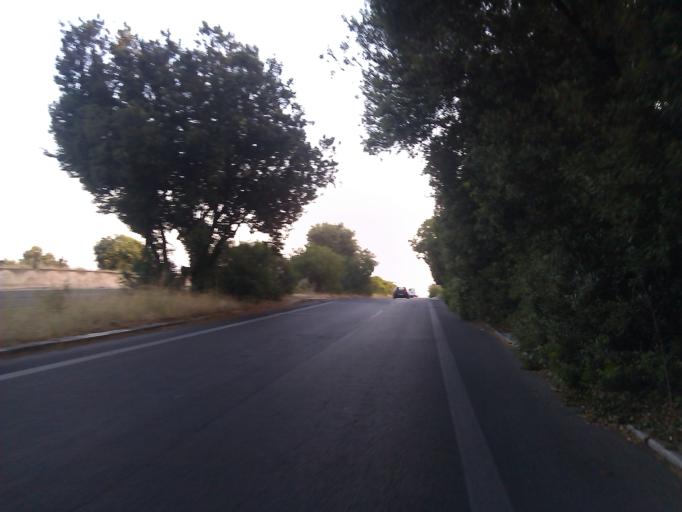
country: IT
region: Latium
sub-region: Citta metropolitana di Roma Capitale
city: Lido di Ostia
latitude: 41.7167
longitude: 12.3198
